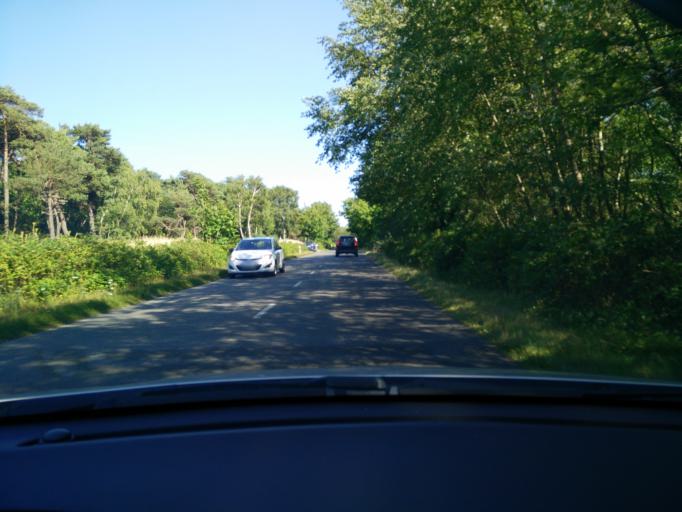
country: PL
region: Pomeranian Voivodeship
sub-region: Powiat pucki
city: Jastarnia
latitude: 54.7240
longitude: 18.6130
